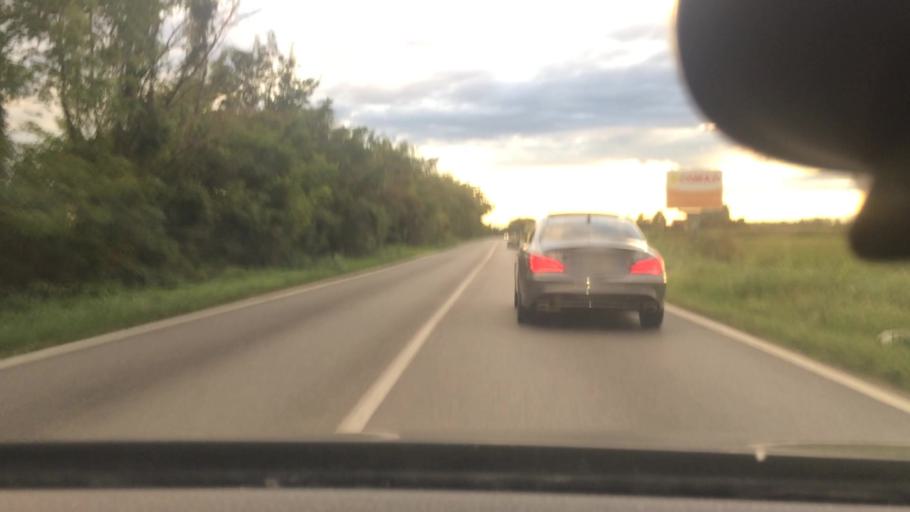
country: IT
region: Lombardy
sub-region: Citta metropolitana di Milano
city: Mantegazza
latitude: 45.5229
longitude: 8.9665
